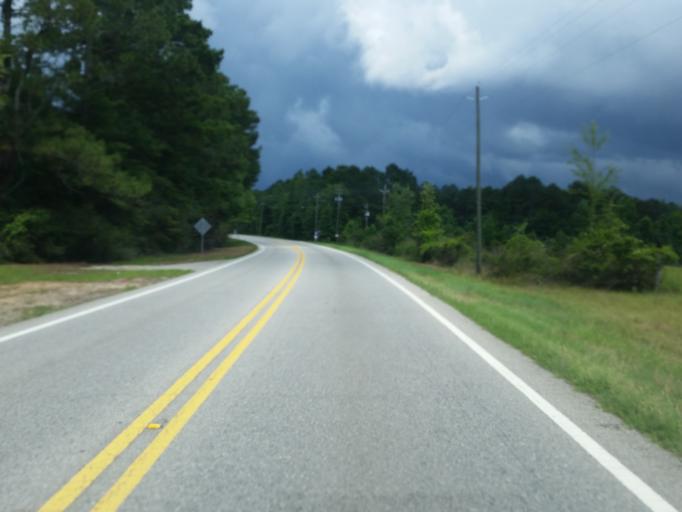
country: US
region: Mississippi
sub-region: Jackson County
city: Hurley
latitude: 30.8270
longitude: -88.3796
